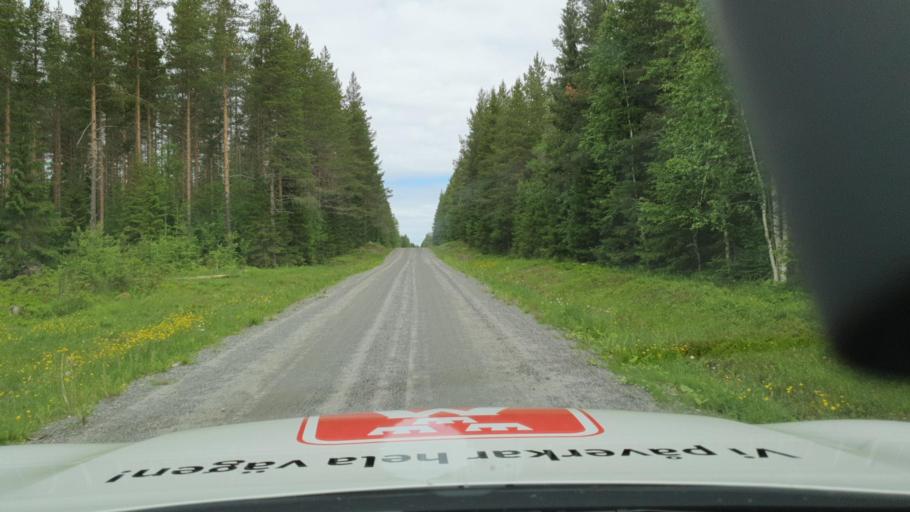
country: SE
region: Vaesterbotten
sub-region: Skelleftea Kommun
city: Burtraesk
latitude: 64.4509
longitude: 20.2980
